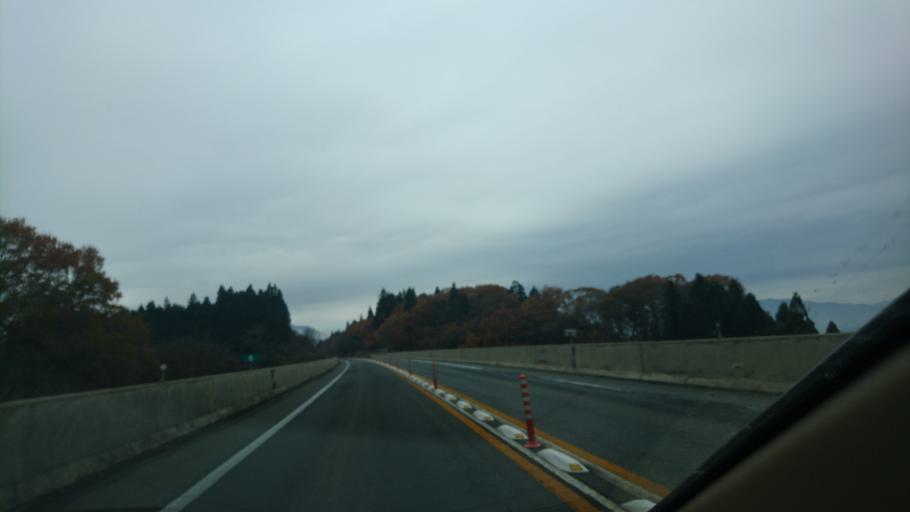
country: JP
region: Iwate
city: Kitakami
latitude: 39.2811
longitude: 141.0118
